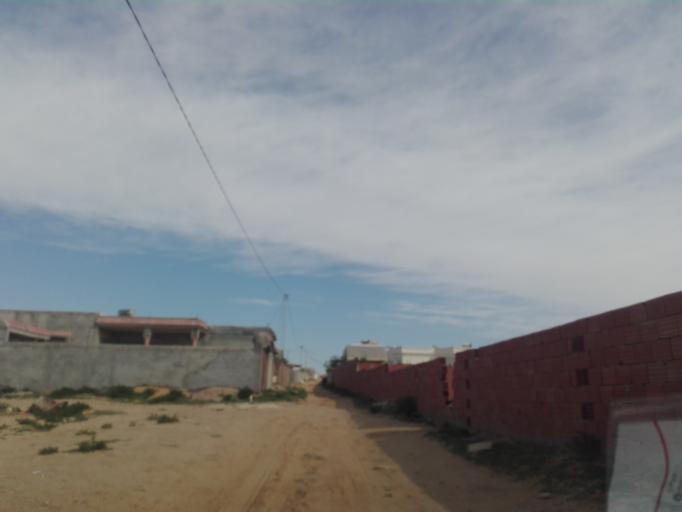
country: TN
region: Safaqis
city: Sfax
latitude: 34.7397
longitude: 10.5116
